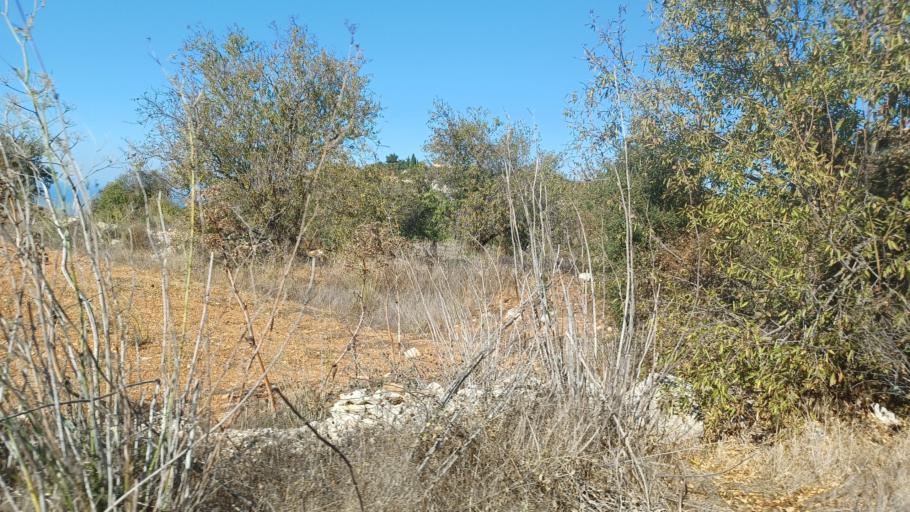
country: CY
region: Pafos
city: Mesogi
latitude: 34.8018
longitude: 32.4887
